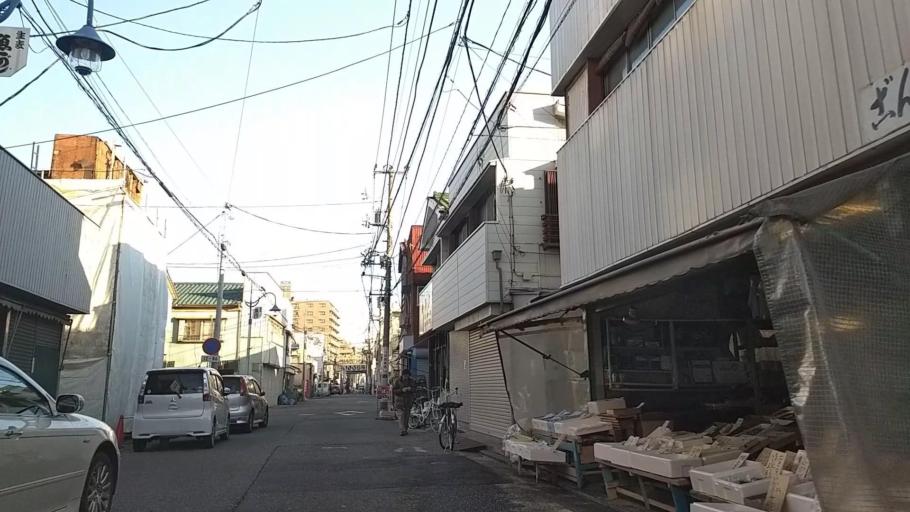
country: JP
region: Kanagawa
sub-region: Kawasaki-shi
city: Kawasaki
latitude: 35.4987
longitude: 139.6752
